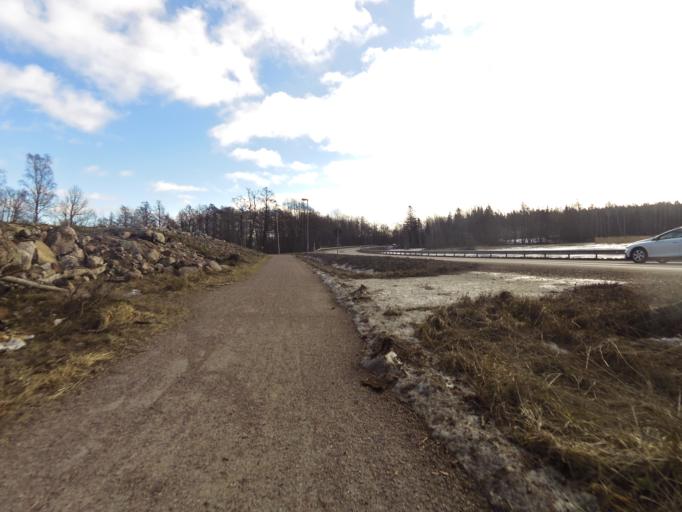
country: SE
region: Uppsala
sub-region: Alvkarleby Kommun
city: Skutskaer
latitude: 60.6488
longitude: 17.3678
